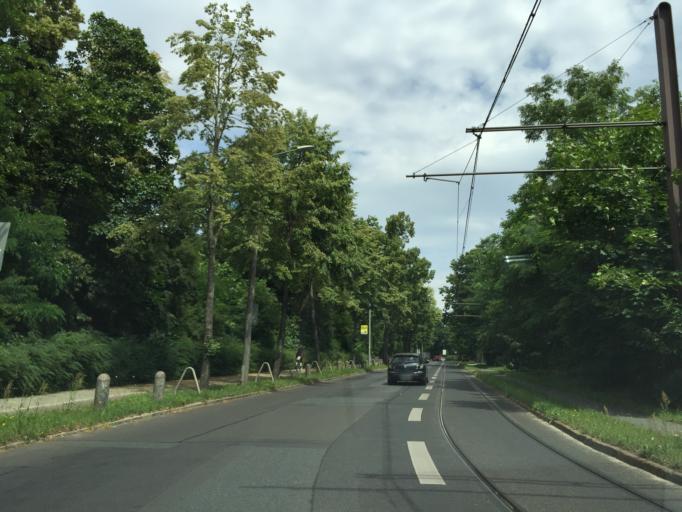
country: DE
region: Berlin
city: Mahlsdorf
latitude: 52.5007
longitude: 13.6132
